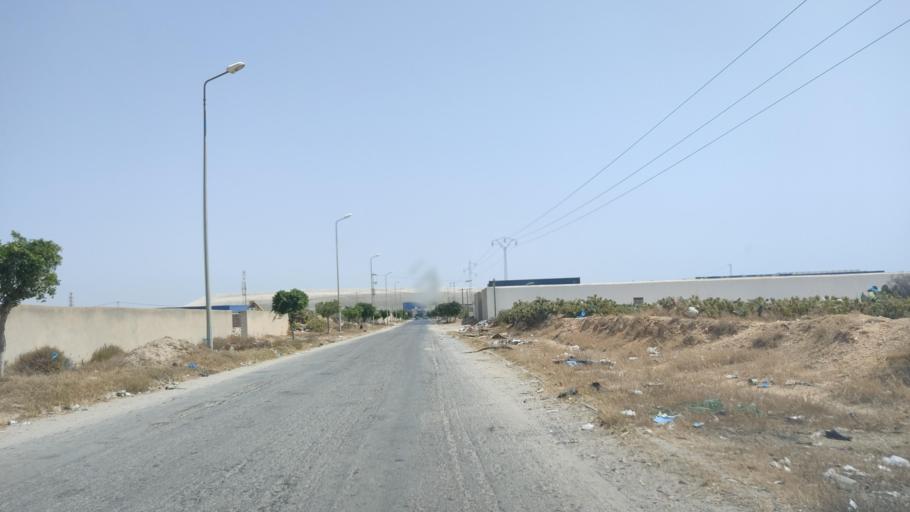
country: TN
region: Safaqis
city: Sfax
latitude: 34.6863
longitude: 10.7240
